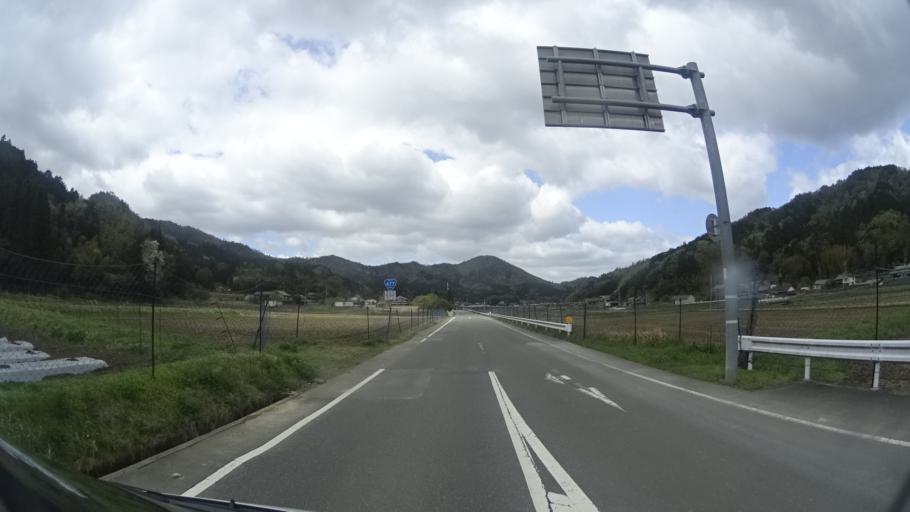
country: JP
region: Kyoto
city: Kameoka
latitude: 35.0839
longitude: 135.4715
